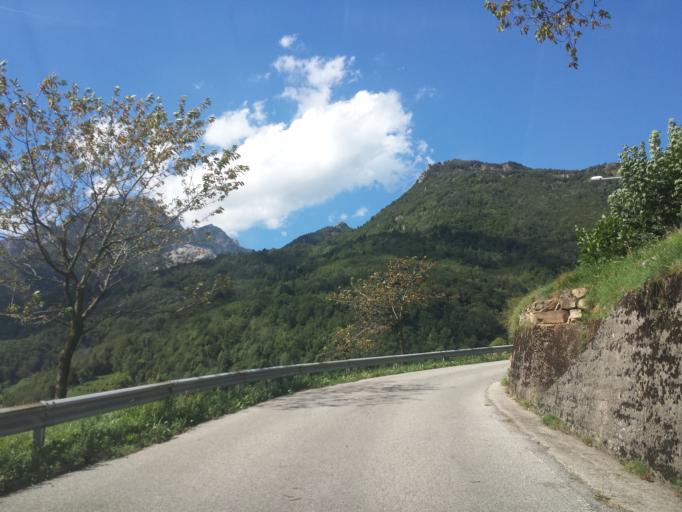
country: IT
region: Veneto
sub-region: Provincia di Vicenza
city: Recoaro Terme
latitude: 45.7144
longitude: 11.2004
